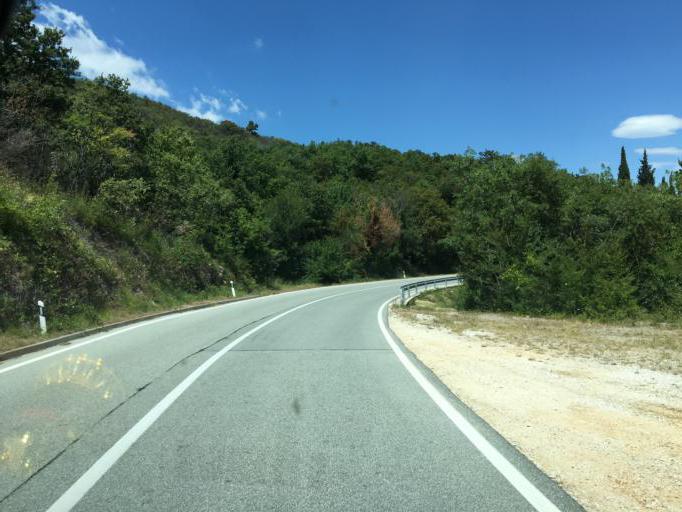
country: HR
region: Istarska
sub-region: Grad Labin
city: Rabac
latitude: 45.1330
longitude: 14.2050
